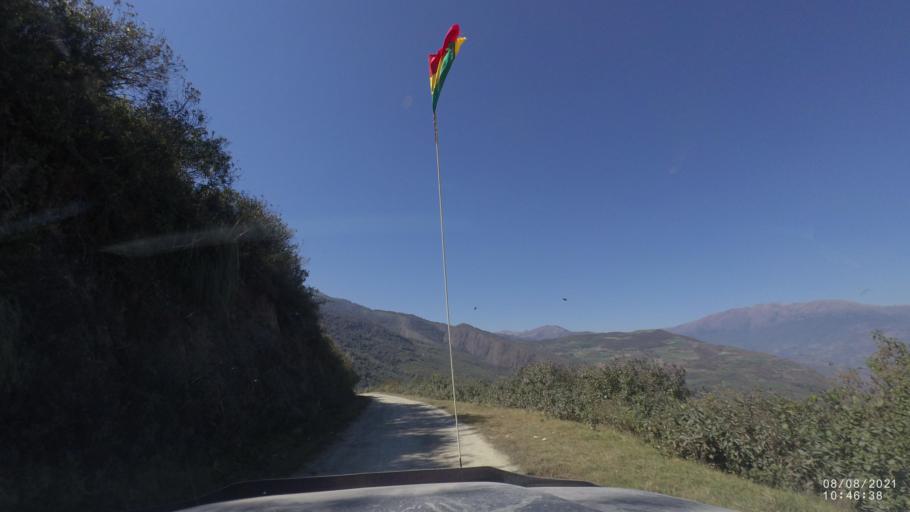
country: BO
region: La Paz
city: Quime
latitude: -16.7093
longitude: -66.7112
